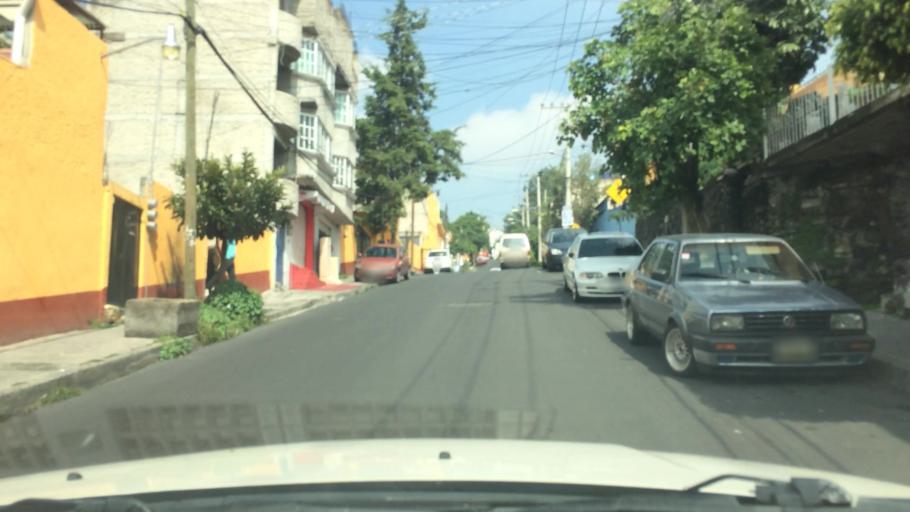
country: MX
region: Mexico City
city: Alvaro Obregon
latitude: 19.3483
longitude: -99.2164
